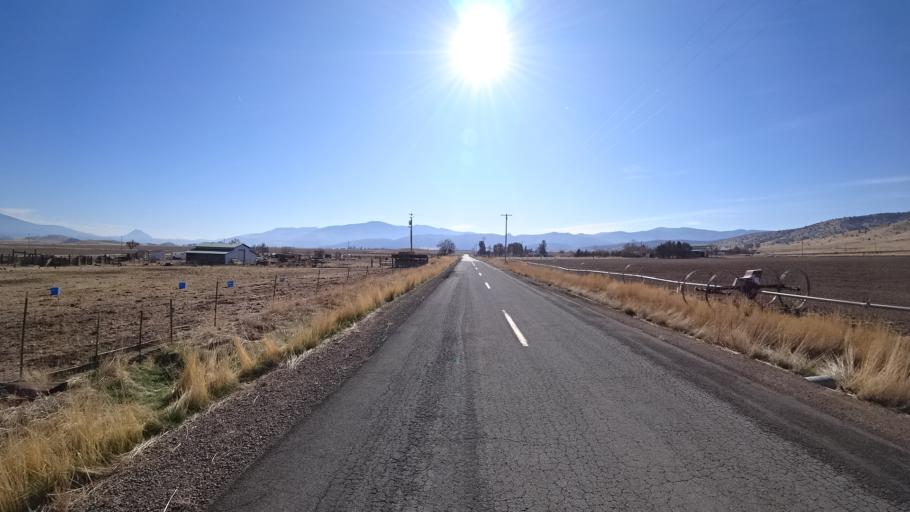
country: US
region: California
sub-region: Siskiyou County
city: Montague
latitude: 41.5773
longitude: -122.5469
